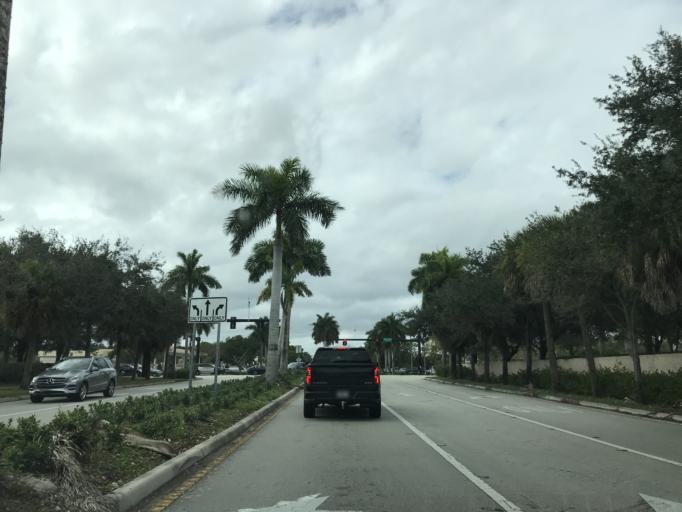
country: US
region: Florida
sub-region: Broward County
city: Coral Springs
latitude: 26.3064
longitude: -80.2779
